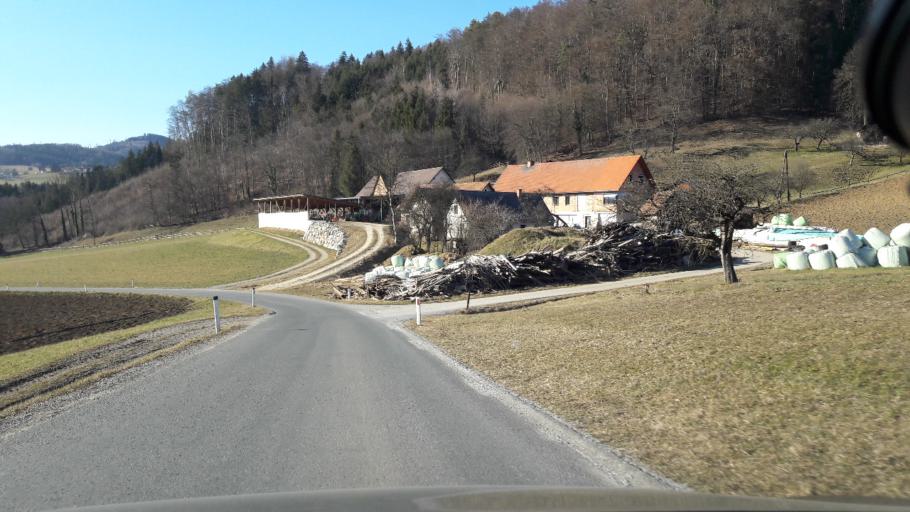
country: AT
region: Styria
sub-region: Politischer Bezirk Graz-Umgebung
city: Eisbach
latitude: 47.1127
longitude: 15.2771
